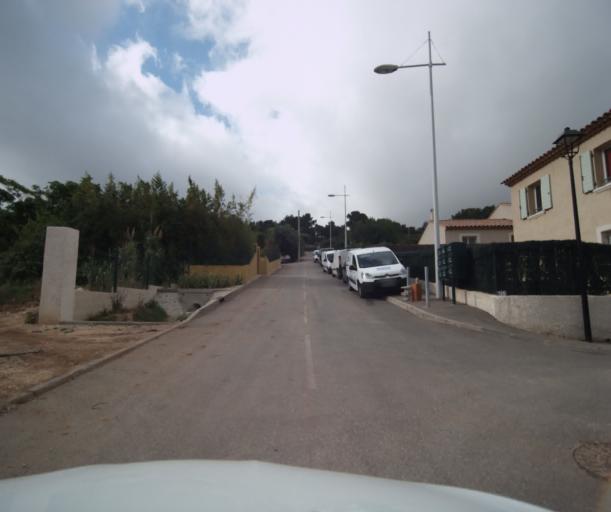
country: FR
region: Provence-Alpes-Cote d'Azur
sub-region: Departement du Var
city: Ollioules
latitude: 43.1264
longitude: 5.8537
